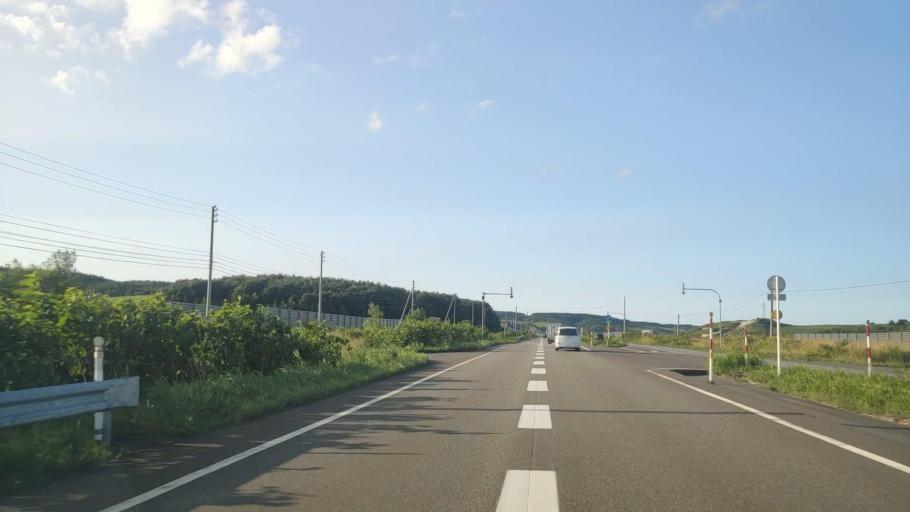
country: JP
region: Hokkaido
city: Wakkanai
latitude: 45.3224
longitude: 141.7194
